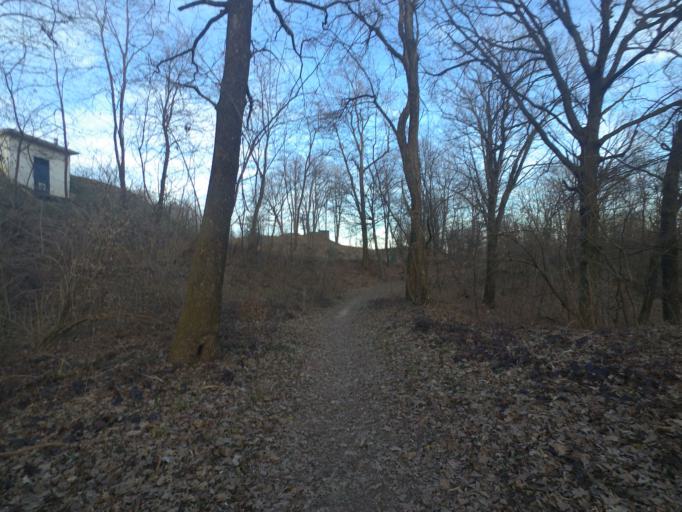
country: HR
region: Karlovacka
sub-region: Grad Karlovac
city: Karlovac
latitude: 45.4744
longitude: 15.5334
